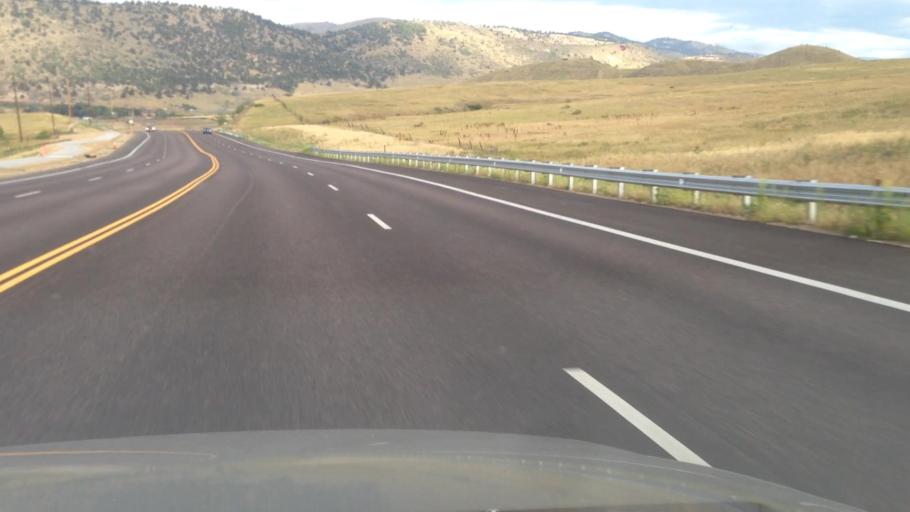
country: US
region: Colorado
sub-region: Jefferson County
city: West Pleasant View
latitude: 39.6824
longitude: -105.1756
